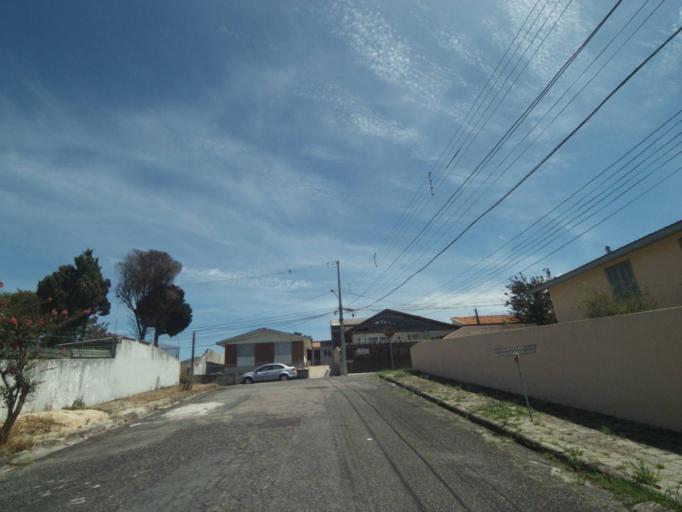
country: BR
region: Parana
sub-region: Curitiba
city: Curitiba
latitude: -25.4651
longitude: -49.2397
